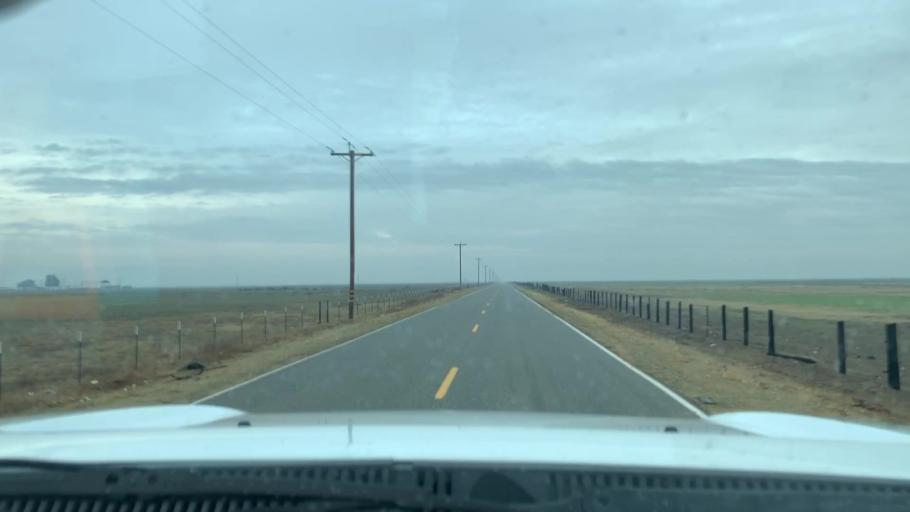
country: US
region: California
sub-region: Kern County
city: Lost Hills
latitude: 35.6761
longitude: -119.5799
